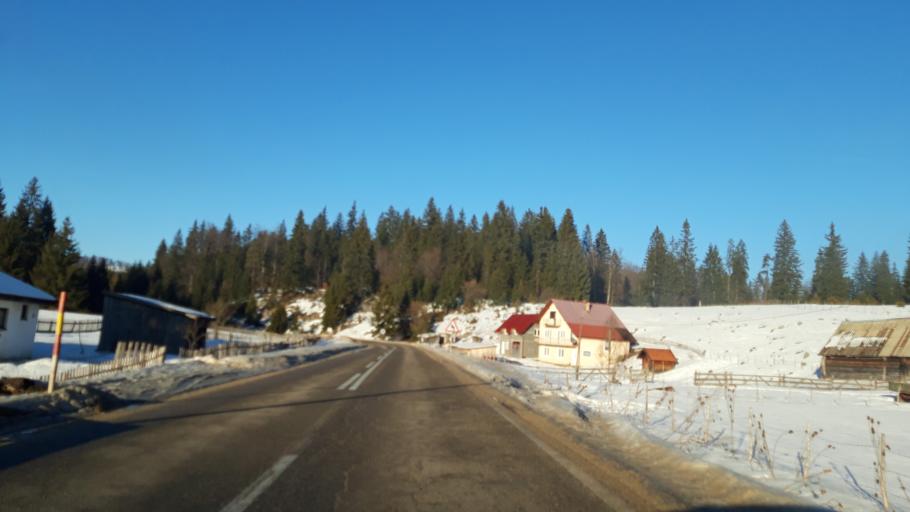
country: BA
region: Republika Srpska
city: Han Pijesak
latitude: 44.1142
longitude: 18.9701
